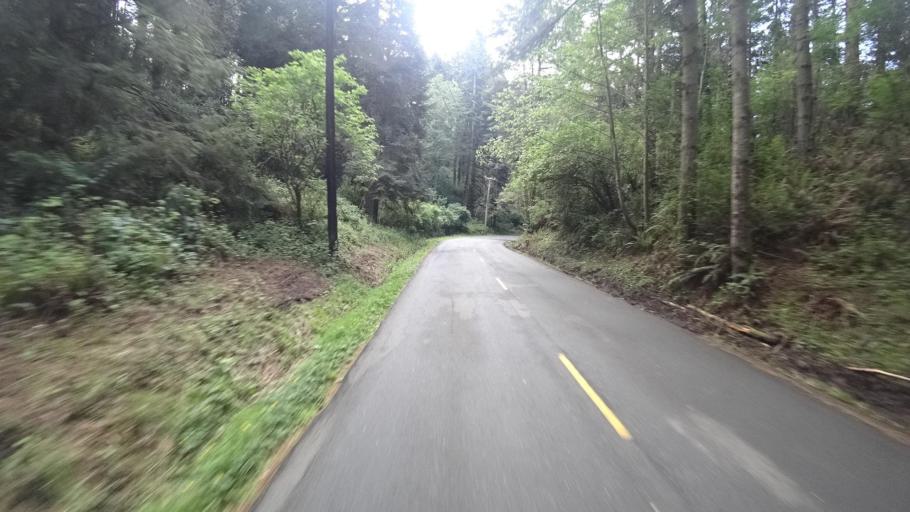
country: US
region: California
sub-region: Humboldt County
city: McKinleyville
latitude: 40.9217
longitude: -124.0790
